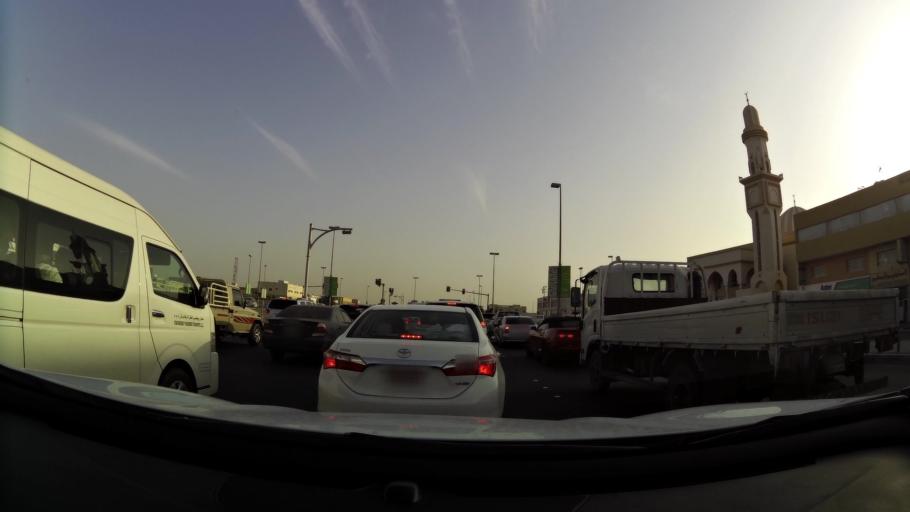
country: AE
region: Abu Dhabi
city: Abu Dhabi
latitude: 24.3742
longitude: 54.5108
